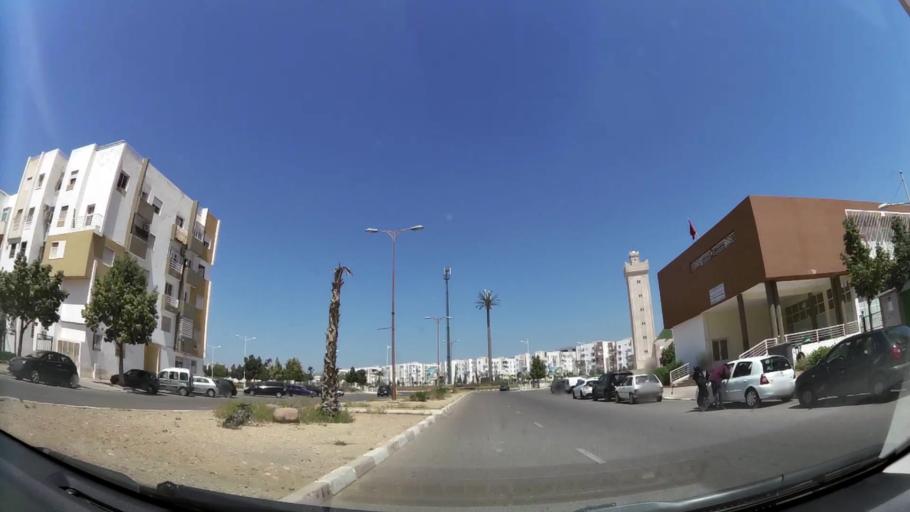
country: MA
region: Oued ed Dahab-Lagouira
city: Dakhla
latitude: 30.4329
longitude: -9.5567
